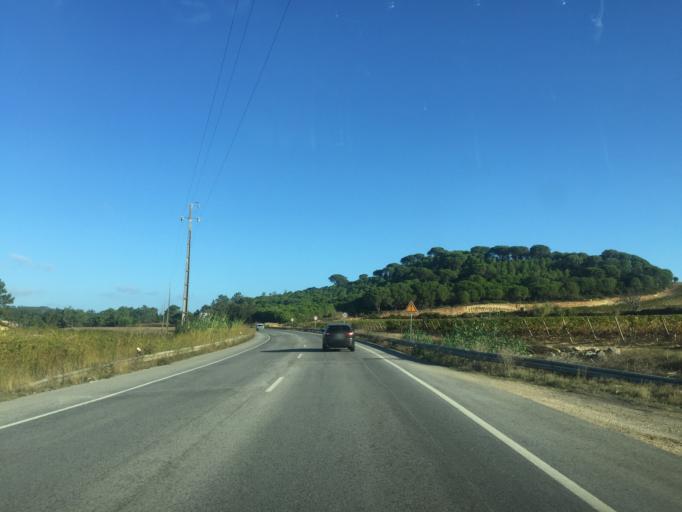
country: PT
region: Lisbon
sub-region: Azambuja
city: Alcoentre
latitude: 39.2149
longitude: -8.9536
